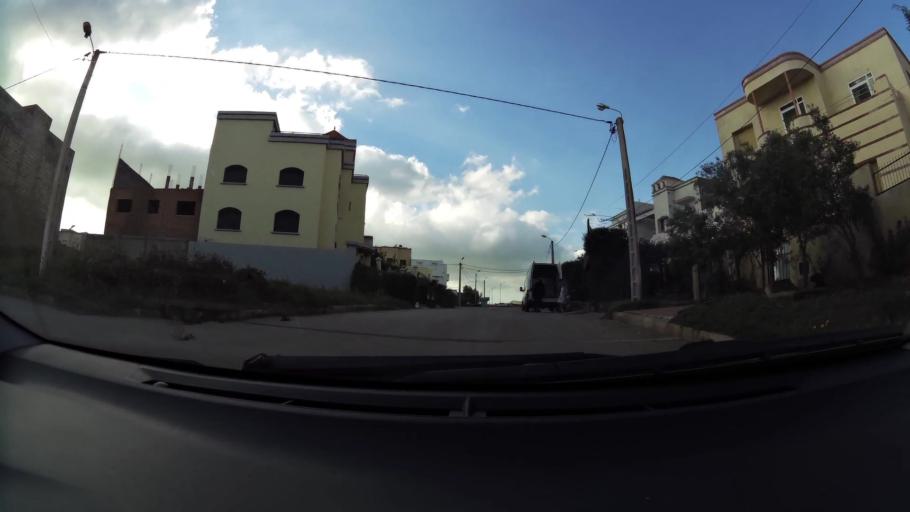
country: MA
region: Chaouia-Ouardigha
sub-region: Settat Province
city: Settat
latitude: 33.0084
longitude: -7.6372
